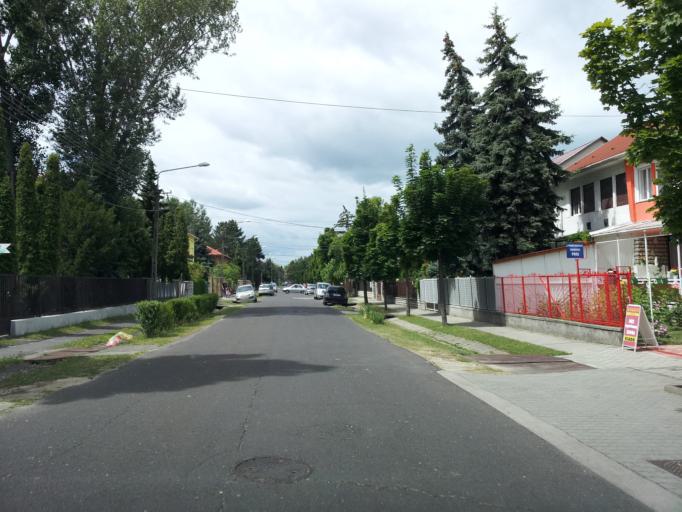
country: HU
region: Somogy
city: Siofok
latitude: 46.9157
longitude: 18.0714
